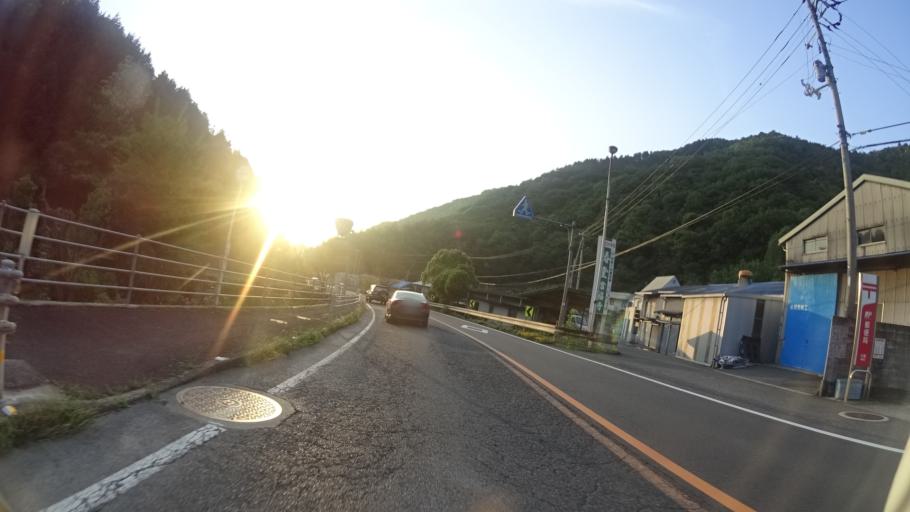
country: JP
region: Ehime
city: Kawanoecho
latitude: 33.9903
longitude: 133.6312
